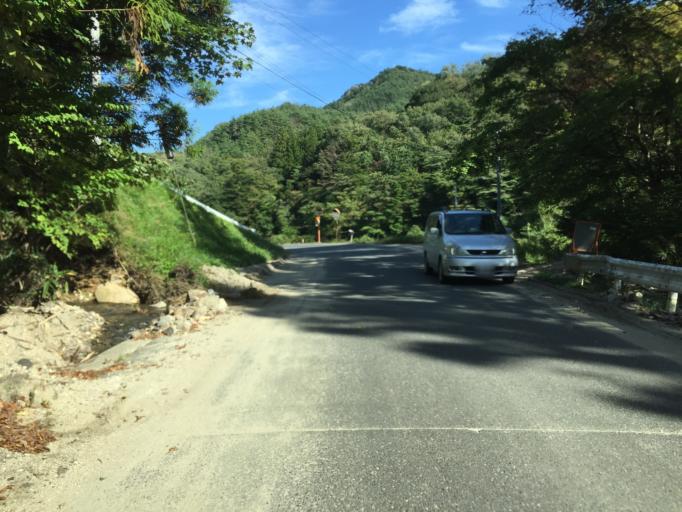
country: JP
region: Miyagi
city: Marumori
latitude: 37.8575
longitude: 140.7546
